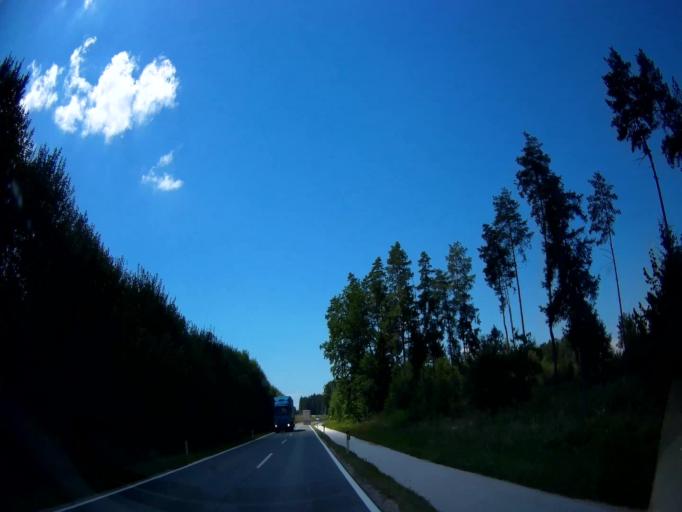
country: AT
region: Carinthia
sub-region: Politischer Bezirk Volkermarkt
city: Eberndorf
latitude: 46.6102
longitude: 14.6788
